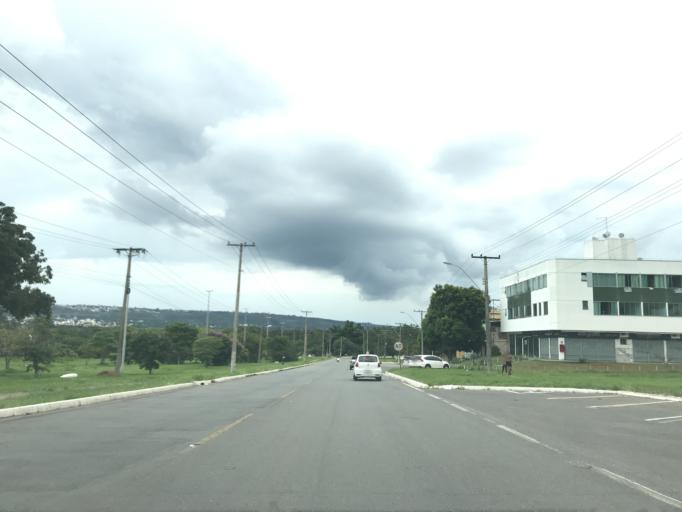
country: BR
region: Federal District
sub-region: Brasilia
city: Brasilia
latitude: -15.6551
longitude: -47.8115
